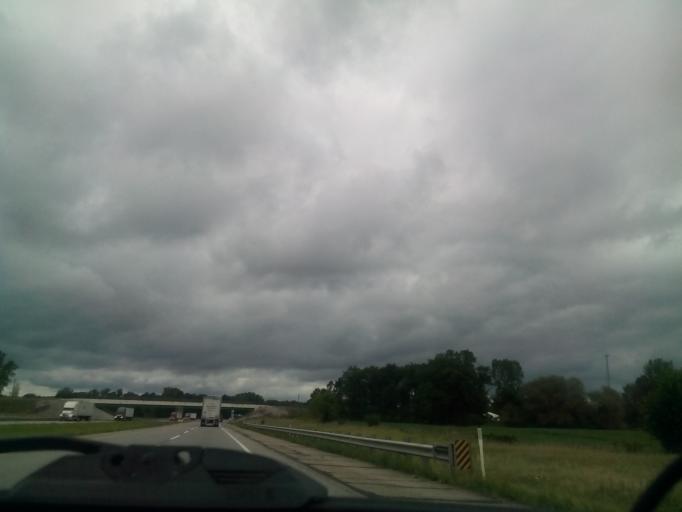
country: US
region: Michigan
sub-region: Branch County
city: Bronson
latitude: 41.7488
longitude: -85.2711
